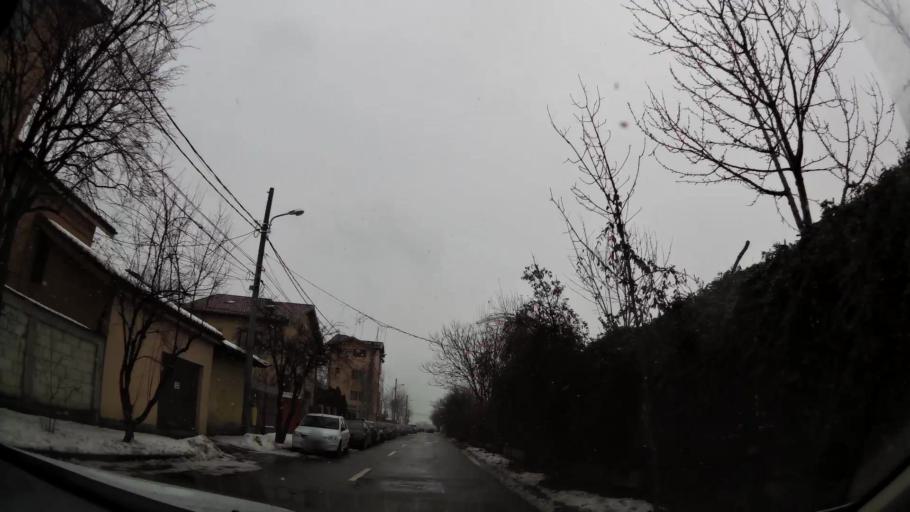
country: RO
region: Ilfov
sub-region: Comuna Mogosoaia
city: Mogosoaia
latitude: 44.4992
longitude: 26.0399
